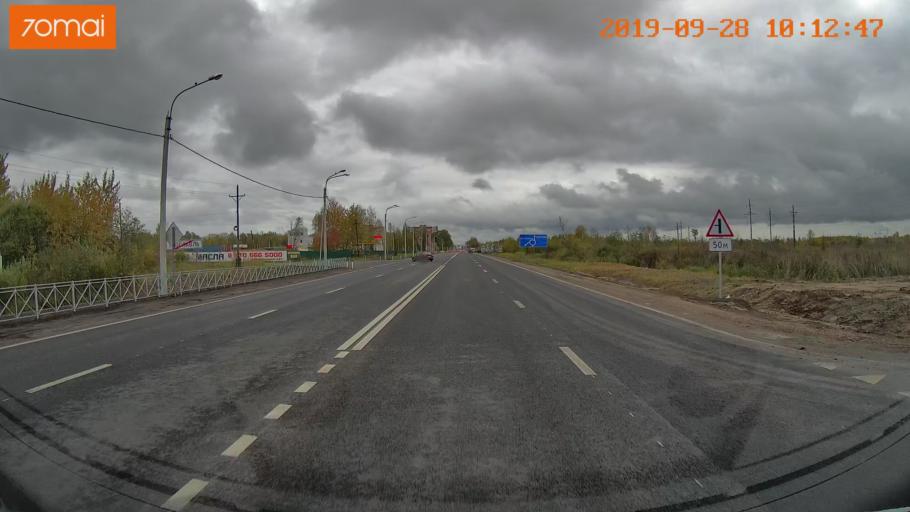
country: RU
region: Jaroslavl
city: Yaroslavl
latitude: 57.5419
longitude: 39.9647
